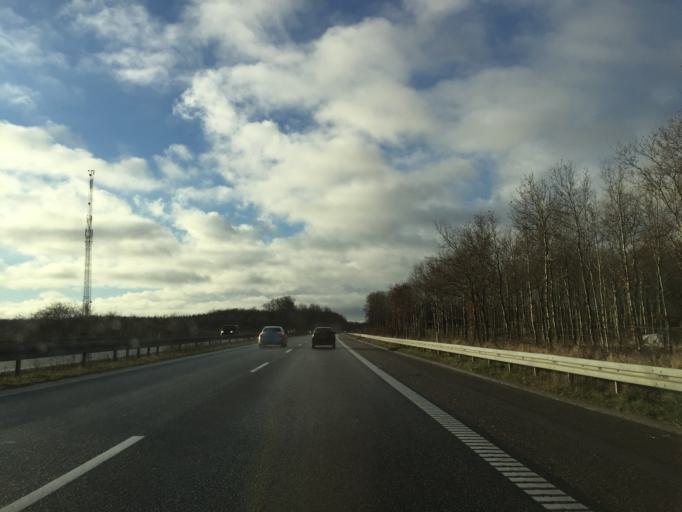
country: DK
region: Zealand
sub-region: Soro Kommune
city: Soro
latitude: 55.4442
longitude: 11.5162
